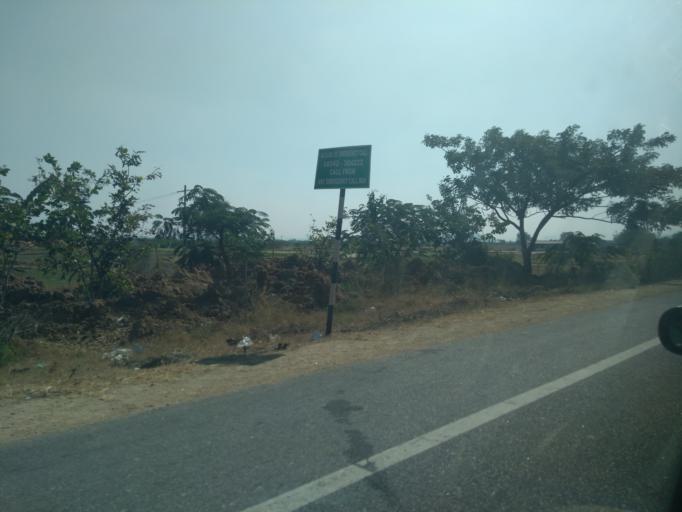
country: IN
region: Telangana
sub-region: Mahbubnagar
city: Mahbubnagar
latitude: 16.6762
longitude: 78.0271
